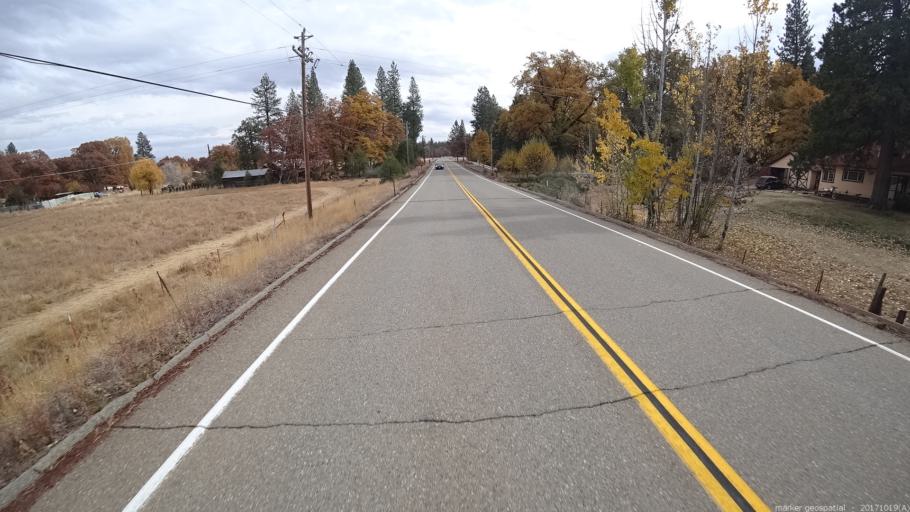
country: US
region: California
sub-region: Shasta County
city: Burney
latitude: 41.0964
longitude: -121.5547
